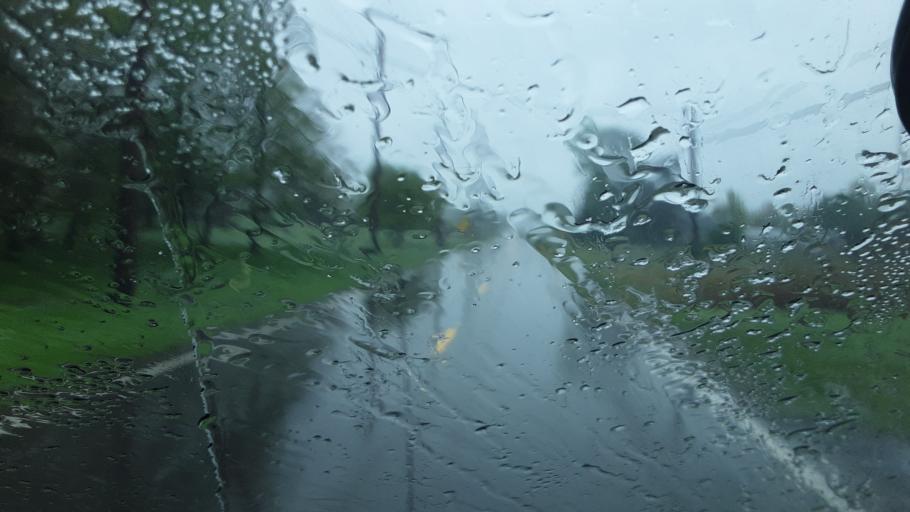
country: US
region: Ohio
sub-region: Portage County
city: Windham
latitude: 41.3084
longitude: -80.9682
